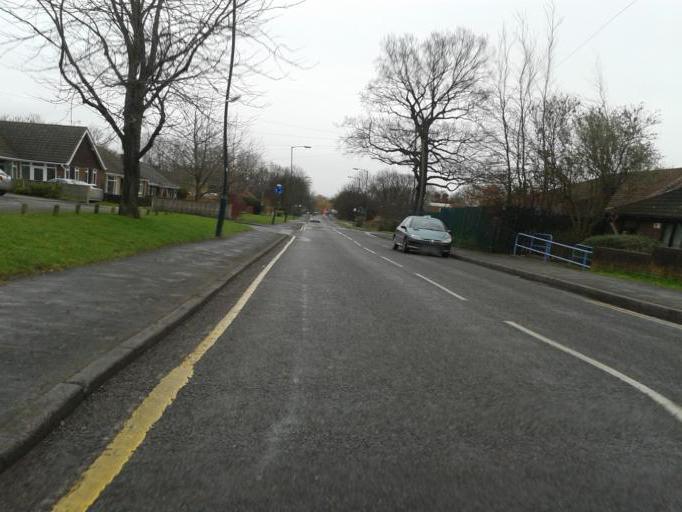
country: GB
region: England
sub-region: Warwickshire
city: Atherstone
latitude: 52.5786
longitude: -1.5429
